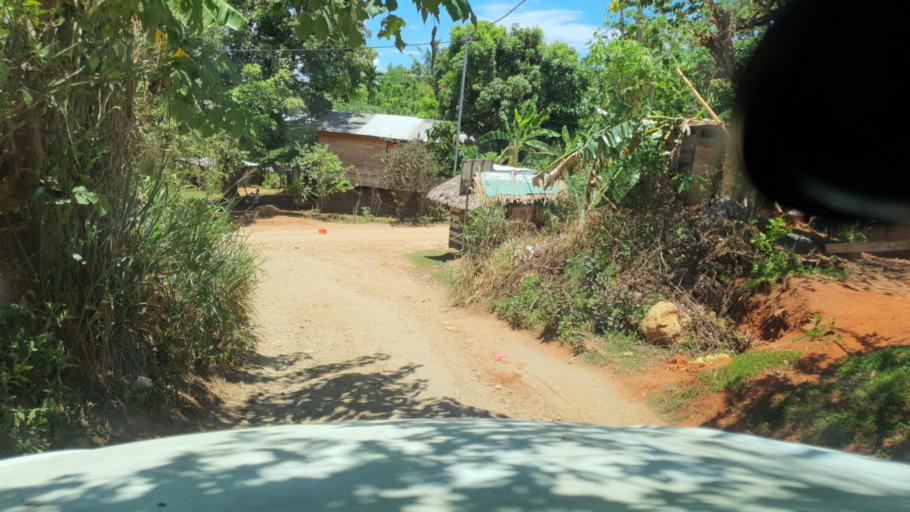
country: SB
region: Guadalcanal
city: Honiara
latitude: -9.4540
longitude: 159.9931
